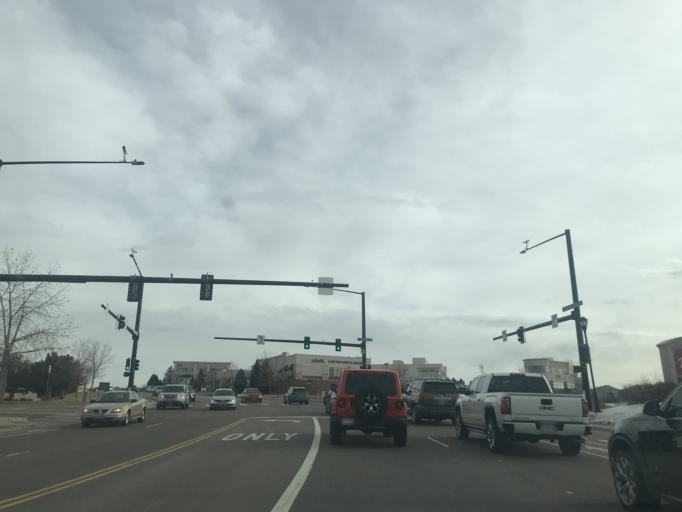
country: US
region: Colorado
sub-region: Adams County
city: Lone Tree
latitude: 39.5540
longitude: -104.8810
